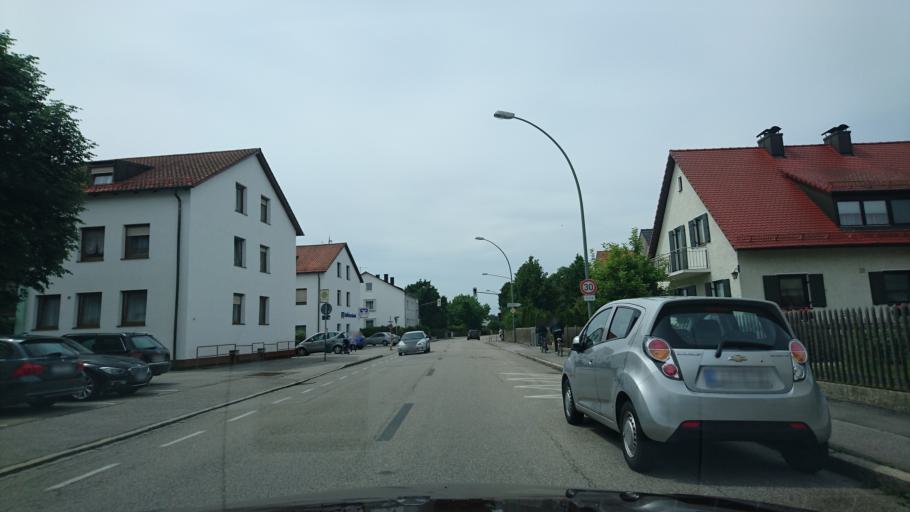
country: DE
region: Bavaria
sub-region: Lower Bavaria
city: Landshut
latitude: 48.5537
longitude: 12.1350
